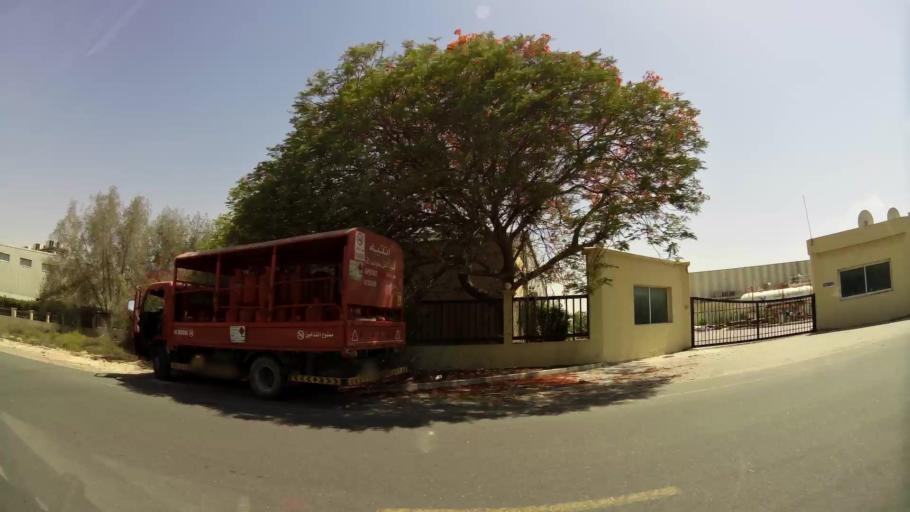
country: AE
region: Dubai
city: Dubai
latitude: 24.9854
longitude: 55.1584
